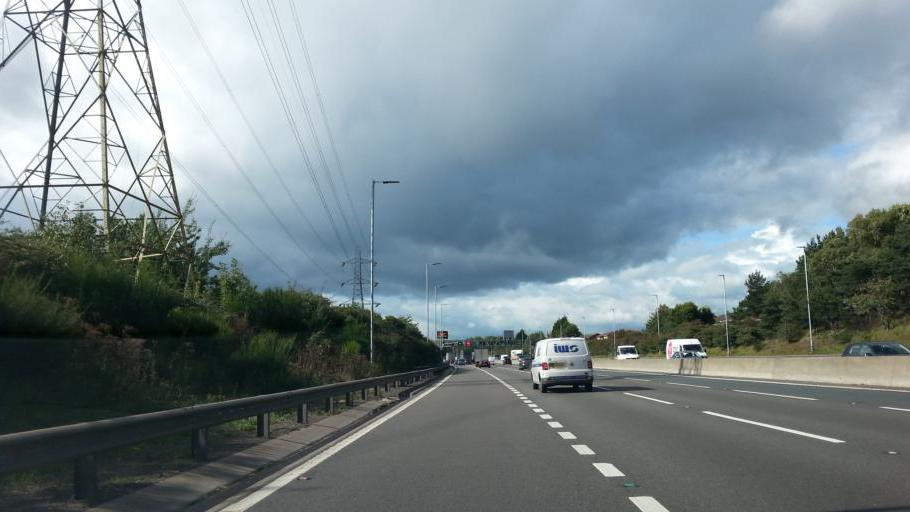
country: GB
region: England
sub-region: City and Borough of Birmingham
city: Birmingham
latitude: 52.5166
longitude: -1.8701
